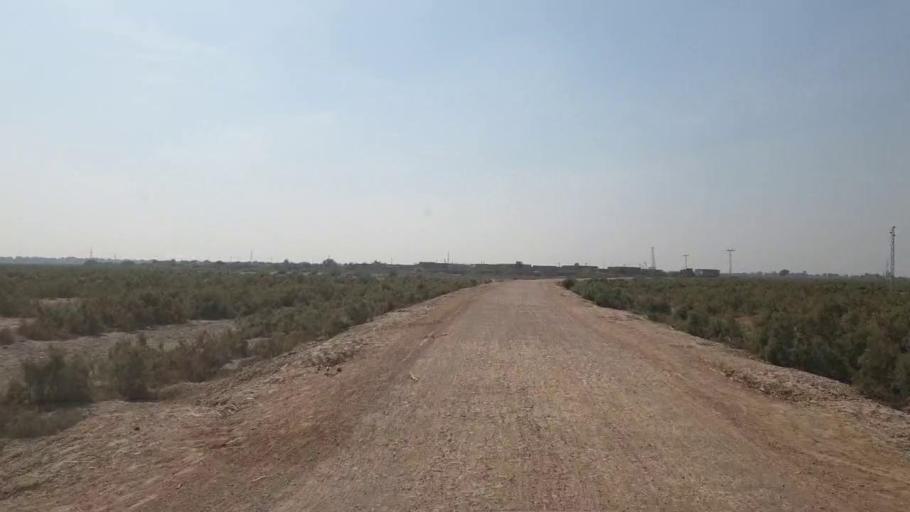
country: PK
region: Sindh
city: Chambar
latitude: 25.3356
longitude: 68.8087
